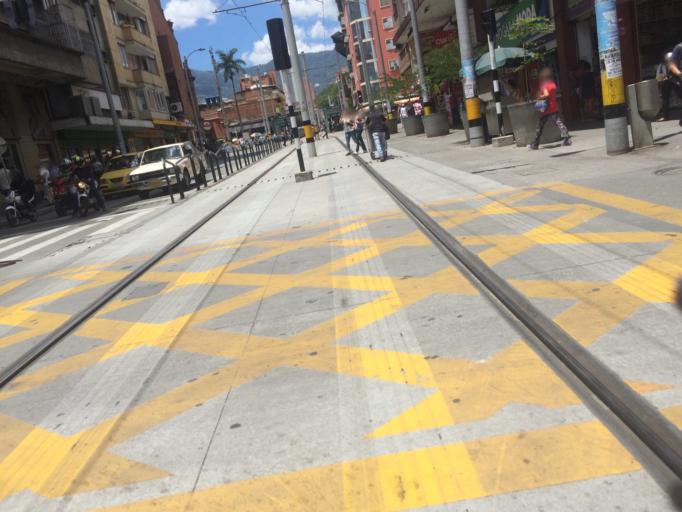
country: CO
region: Antioquia
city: Medellin
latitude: 6.2479
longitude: -75.5666
